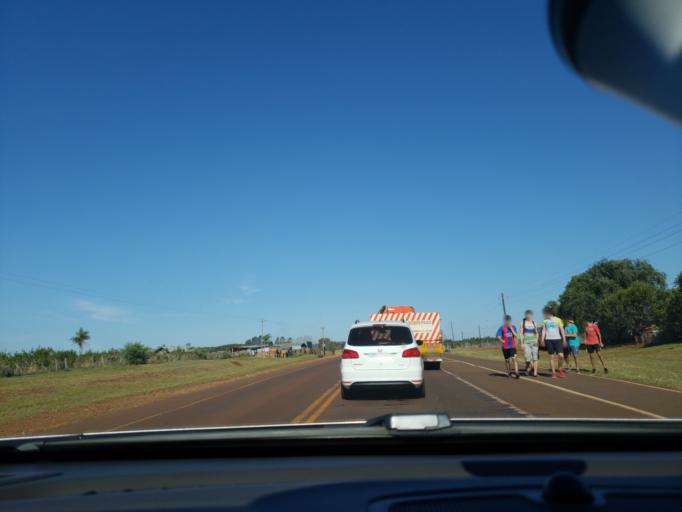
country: AR
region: Misiones
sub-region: Departamento de Apostoles
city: San Jose
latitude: -27.7571
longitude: -55.7747
